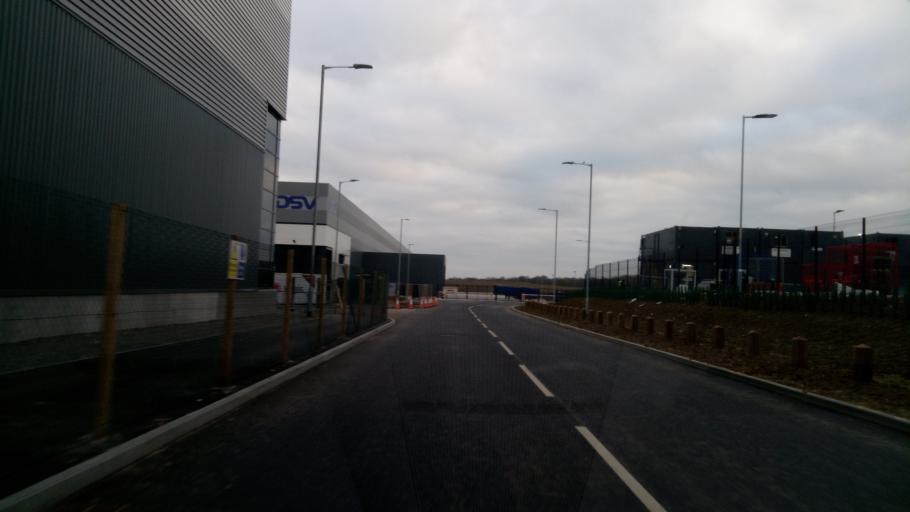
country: GB
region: England
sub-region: Cambridgeshire
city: Yaxley
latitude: 52.5326
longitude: -0.2991
